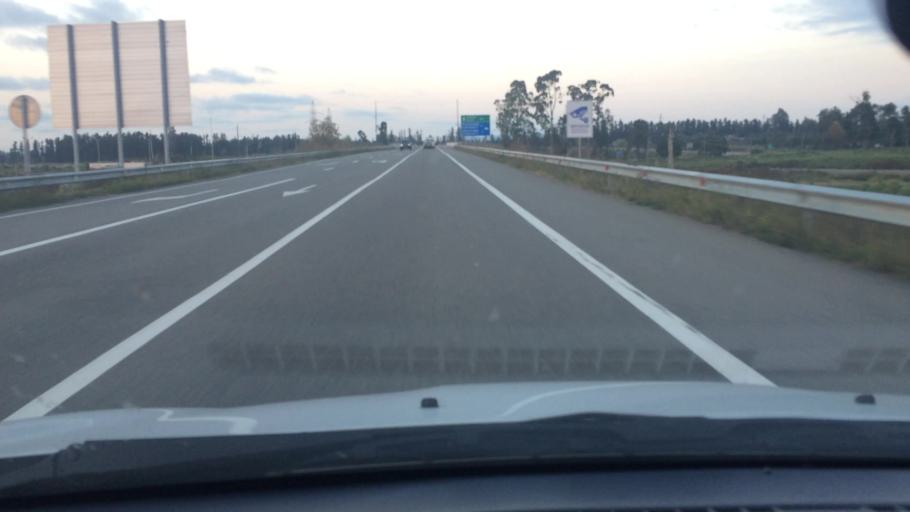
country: GE
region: Ajaria
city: Kobuleti
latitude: 41.8287
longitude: 41.8196
